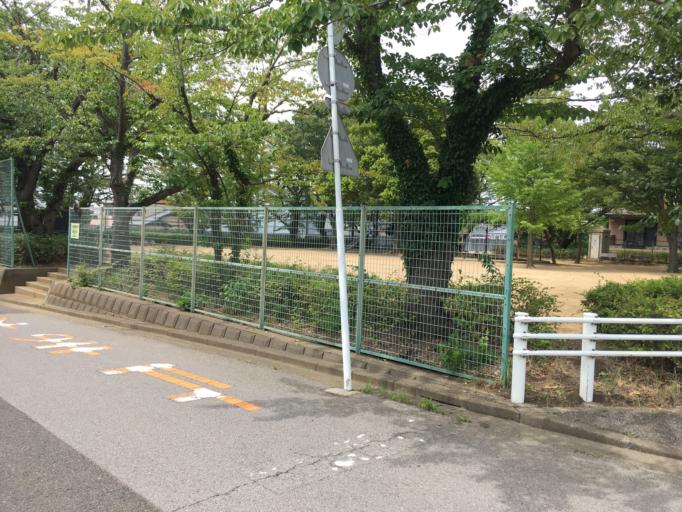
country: JP
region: Chiba
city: Matsudo
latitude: 35.8080
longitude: 139.9337
